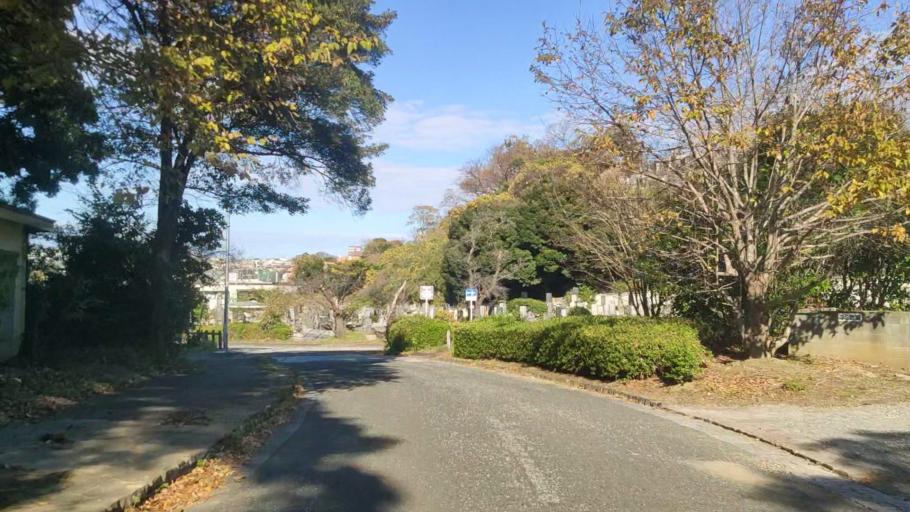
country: JP
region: Kanagawa
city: Yokohama
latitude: 35.3904
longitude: 139.5876
